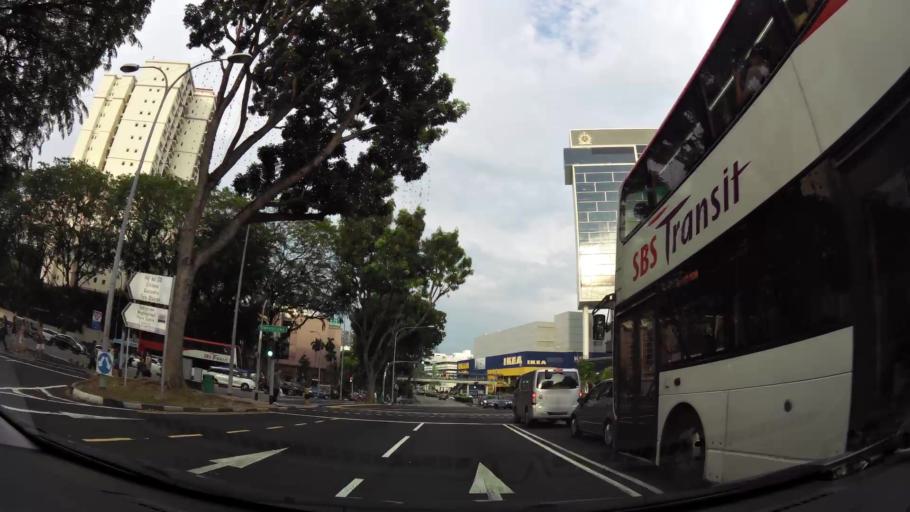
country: SG
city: Singapore
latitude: 1.2874
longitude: 103.8042
